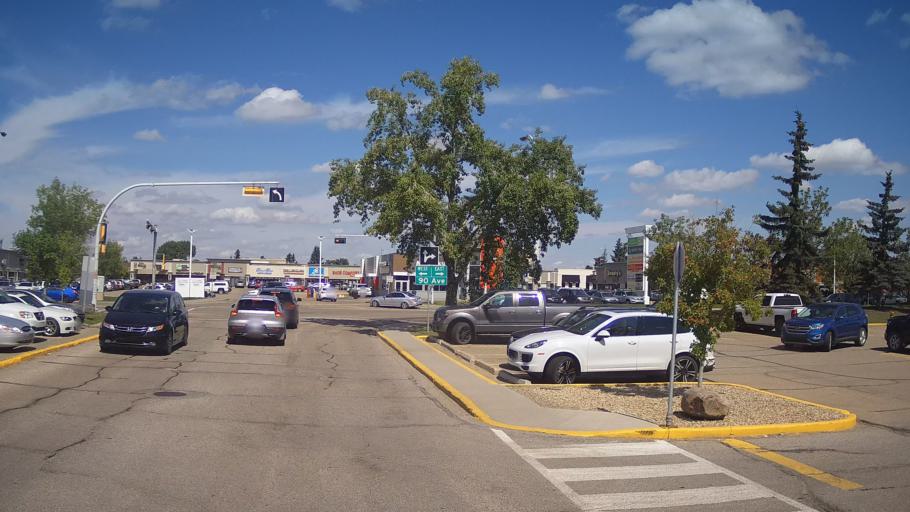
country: CA
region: Alberta
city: St. Albert
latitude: 53.5243
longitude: -113.6179
